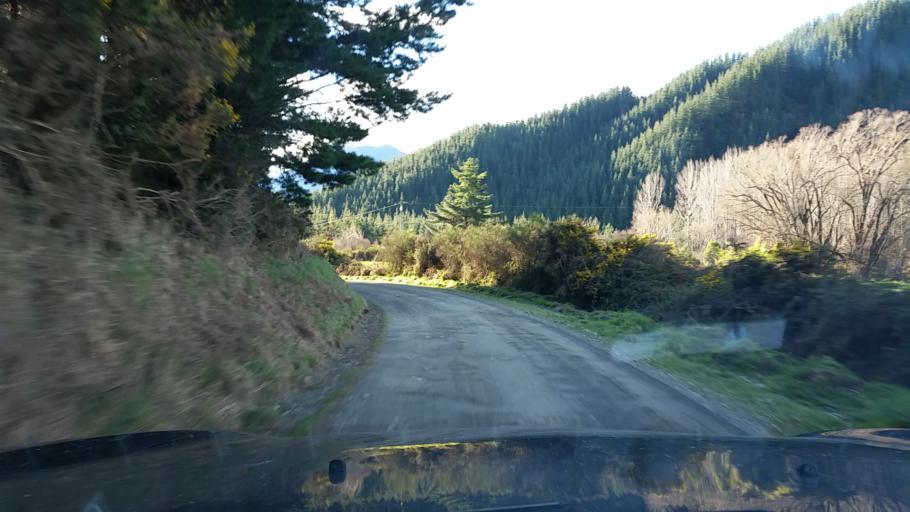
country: NZ
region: Nelson
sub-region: Nelson City
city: Nelson
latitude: -41.5567
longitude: 173.4295
